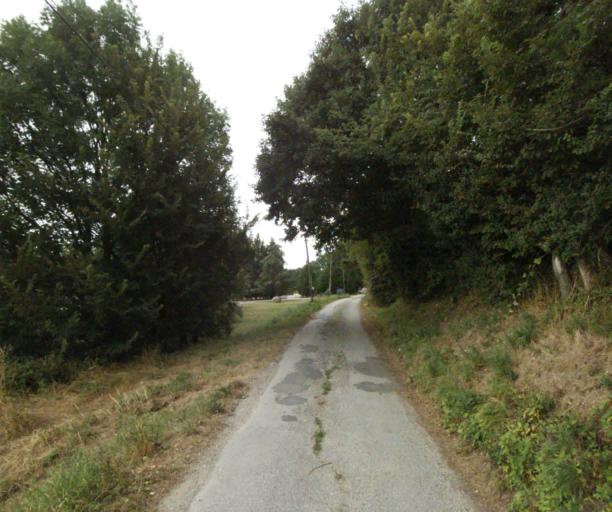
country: FR
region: Midi-Pyrenees
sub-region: Departement du Tarn
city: Soreze
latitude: 43.4470
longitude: 2.0638
